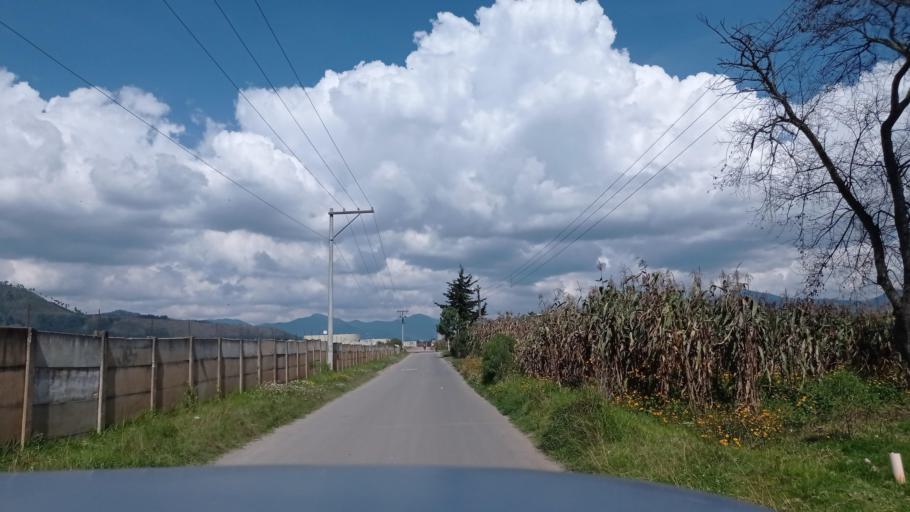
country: GT
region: Quetzaltenango
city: Olintepeque
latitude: 14.8694
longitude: -91.4947
